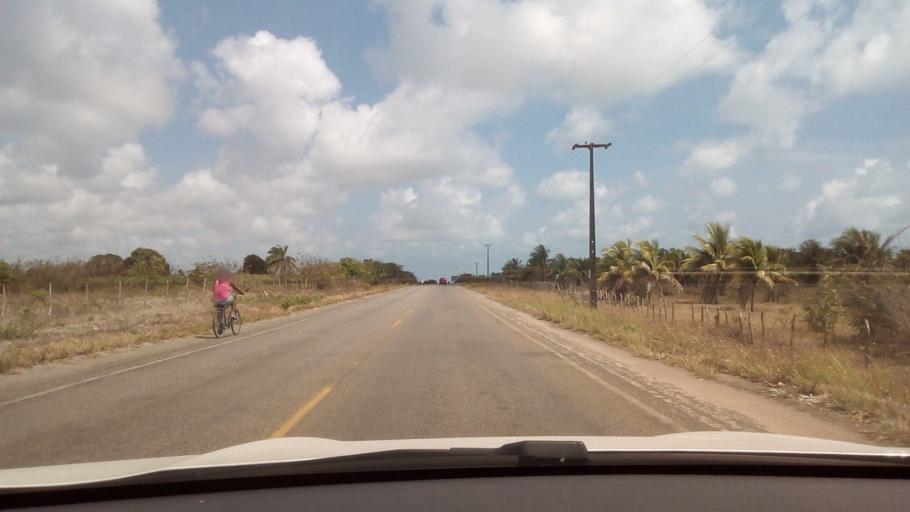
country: BR
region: Paraiba
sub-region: Conde
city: Conde
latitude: -7.2573
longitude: -34.8116
